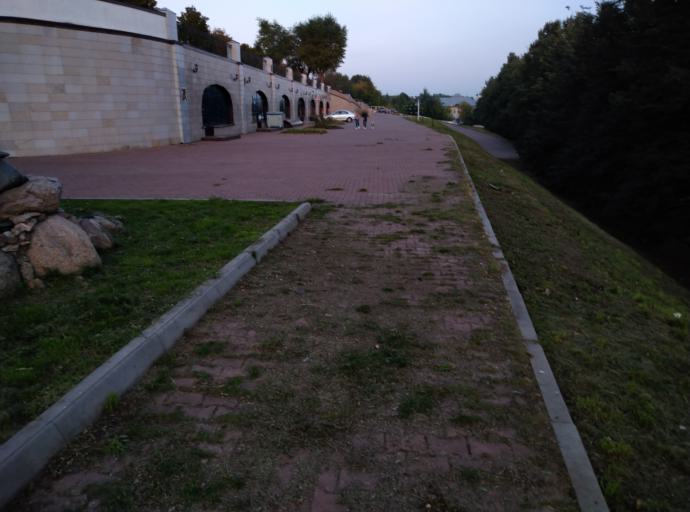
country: RU
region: Kostroma
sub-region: Kostromskoy Rayon
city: Kostroma
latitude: 57.7606
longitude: 40.9374
